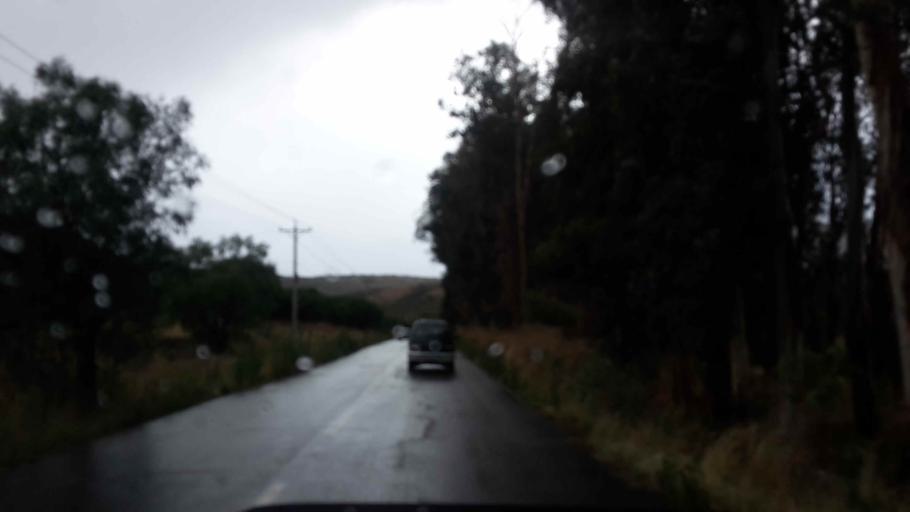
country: BO
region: Cochabamba
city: Tarata
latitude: -17.5402
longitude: -66.1135
